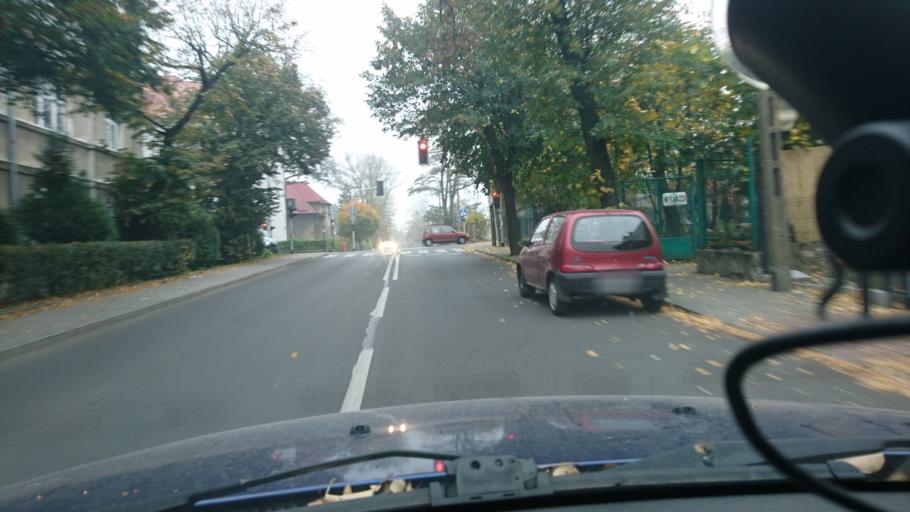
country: PL
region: Silesian Voivodeship
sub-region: Bielsko-Biala
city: Bielsko-Biala
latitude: 49.8240
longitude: 19.0351
